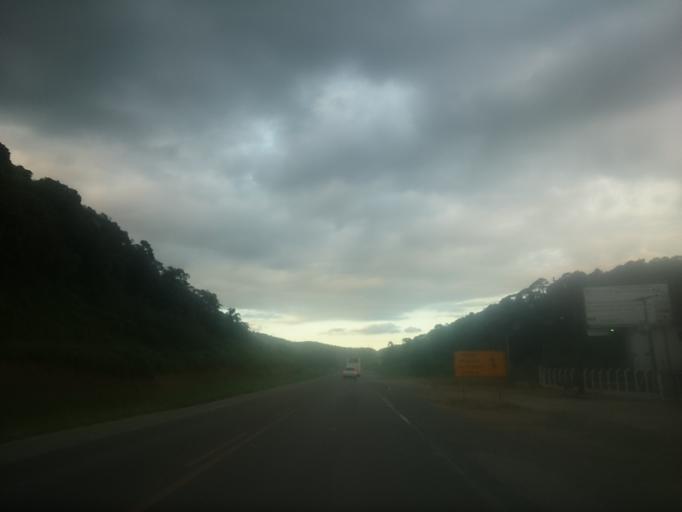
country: BR
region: Santa Catarina
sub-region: Gaspar
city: Gaspar
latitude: -26.9035
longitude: -48.9351
